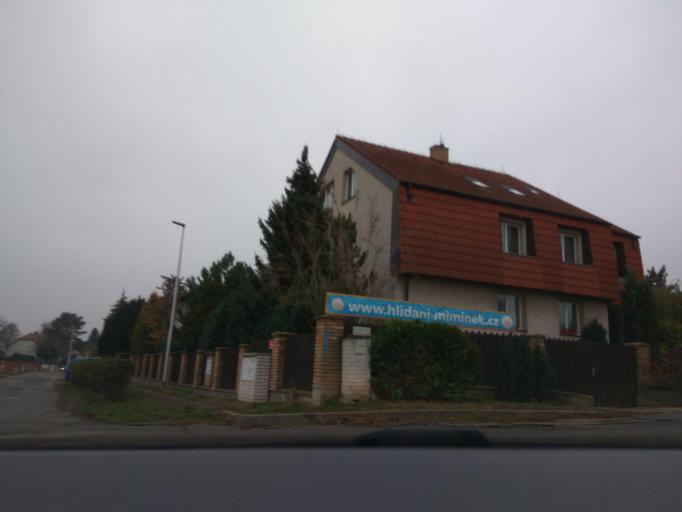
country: CZ
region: Praha
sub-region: Praha 19
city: Kbely
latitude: 50.1606
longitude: 14.5724
